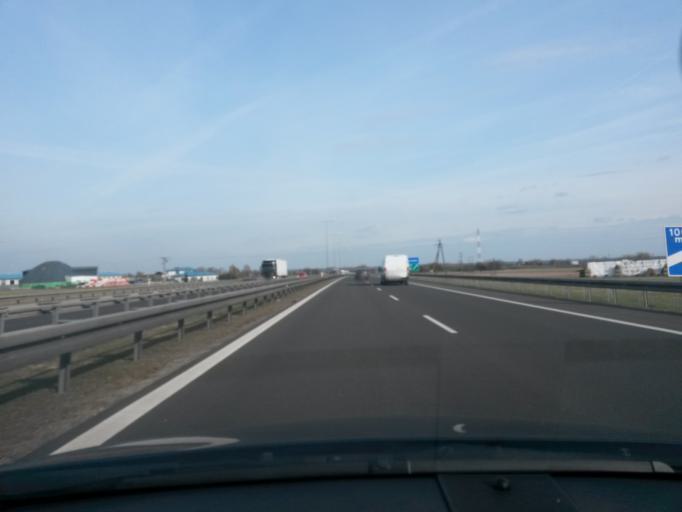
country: PL
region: Greater Poland Voivodeship
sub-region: Powiat koninski
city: Rzgow Pierwszy
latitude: 52.2067
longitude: 18.0144
